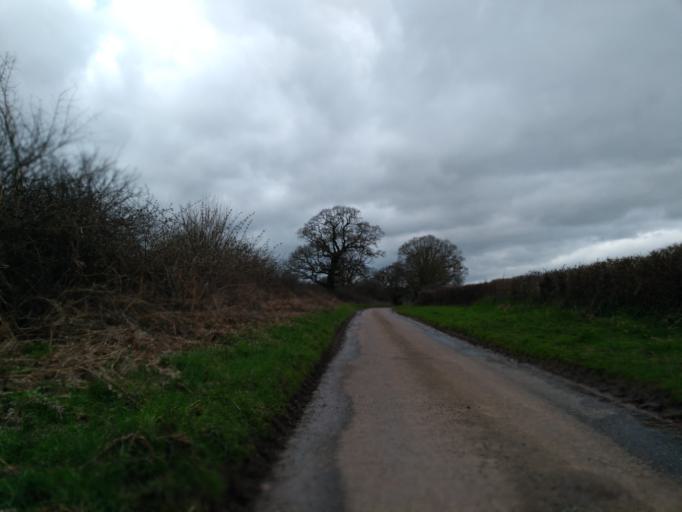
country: GB
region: England
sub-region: Devon
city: Exeter
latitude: 50.7977
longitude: -3.5452
